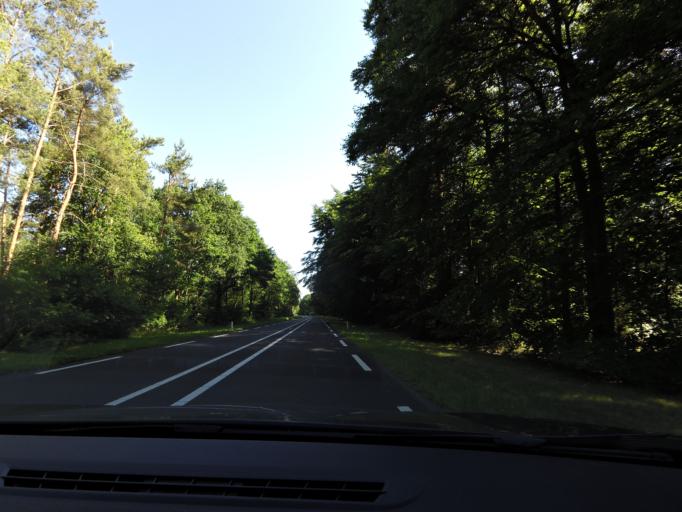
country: NL
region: Overijssel
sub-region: Gemeente Twenterand
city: Den Ham
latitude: 52.4762
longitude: 6.4273
